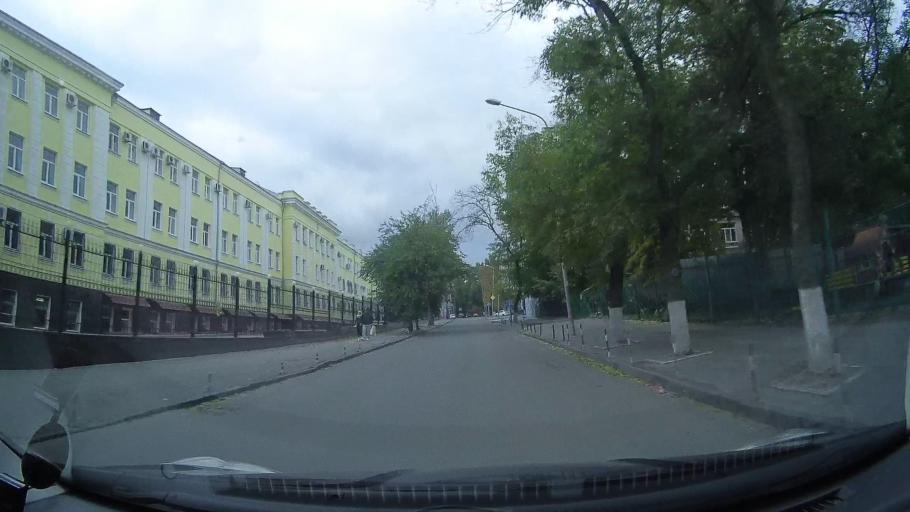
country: RU
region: Rostov
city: Rostov-na-Donu
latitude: 47.2356
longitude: 39.6949
